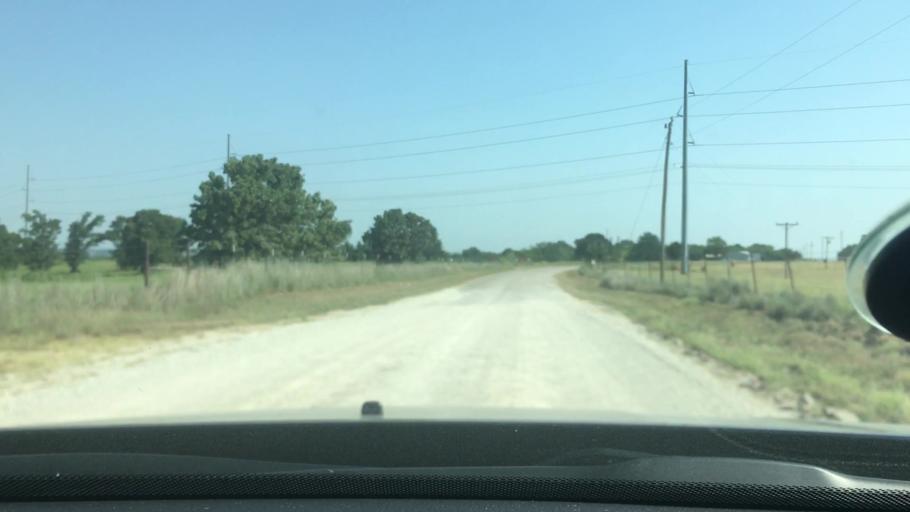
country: US
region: Oklahoma
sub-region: Garvin County
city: Lindsay
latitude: 34.7734
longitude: -97.6120
